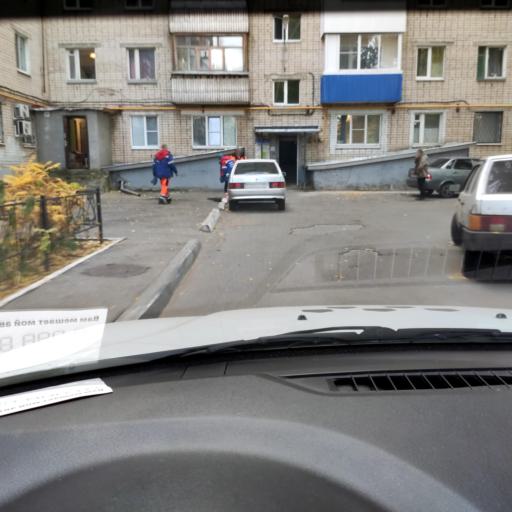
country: RU
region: Samara
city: Tol'yatti
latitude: 53.5184
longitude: 49.4279
